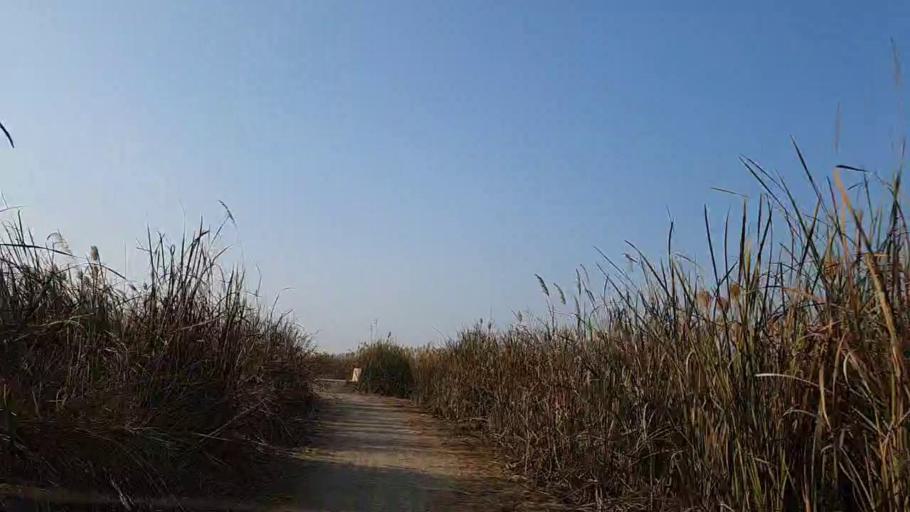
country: PK
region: Sindh
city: Sakrand
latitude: 26.0902
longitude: 68.3829
